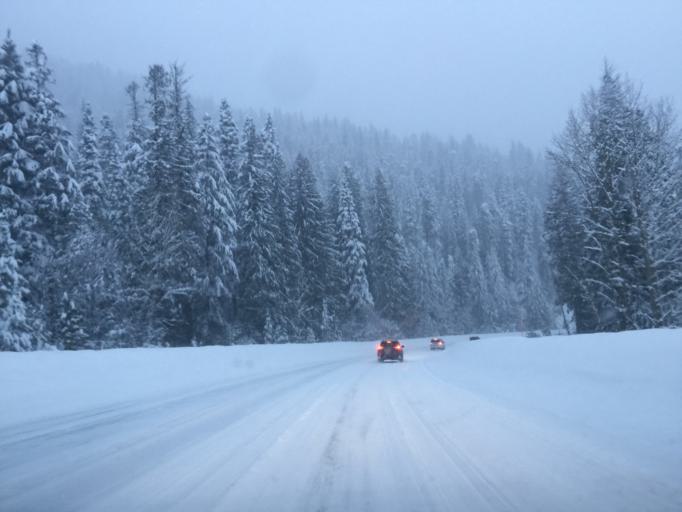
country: US
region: Washington
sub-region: Chelan County
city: Leavenworth
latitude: 47.7859
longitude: -120.8929
